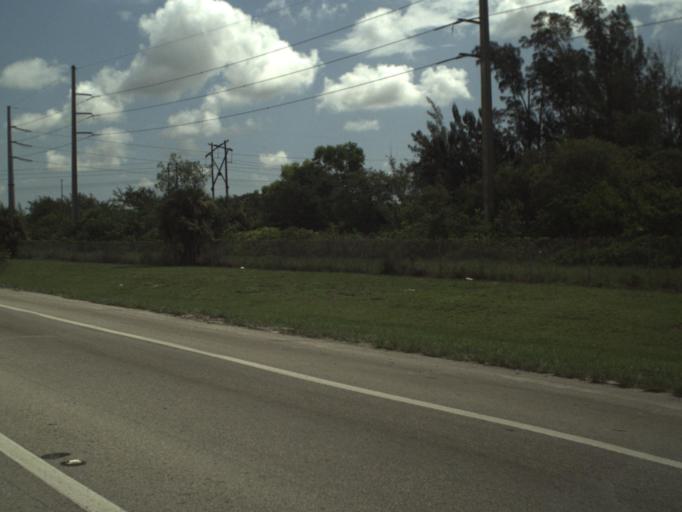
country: US
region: Florida
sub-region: Broward County
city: Broadview Park
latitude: 26.0780
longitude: -80.2048
